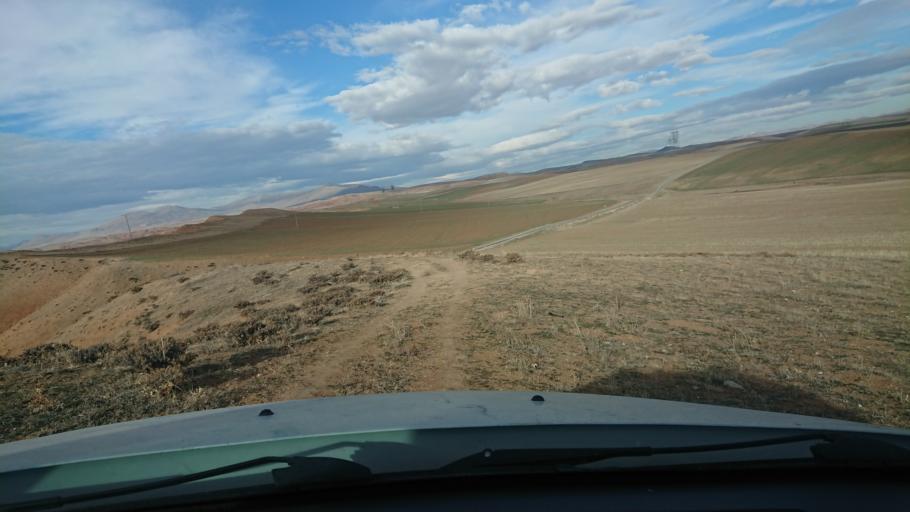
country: TR
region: Aksaray
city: Sariyahsi
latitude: 39.0528
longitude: 33.9798
